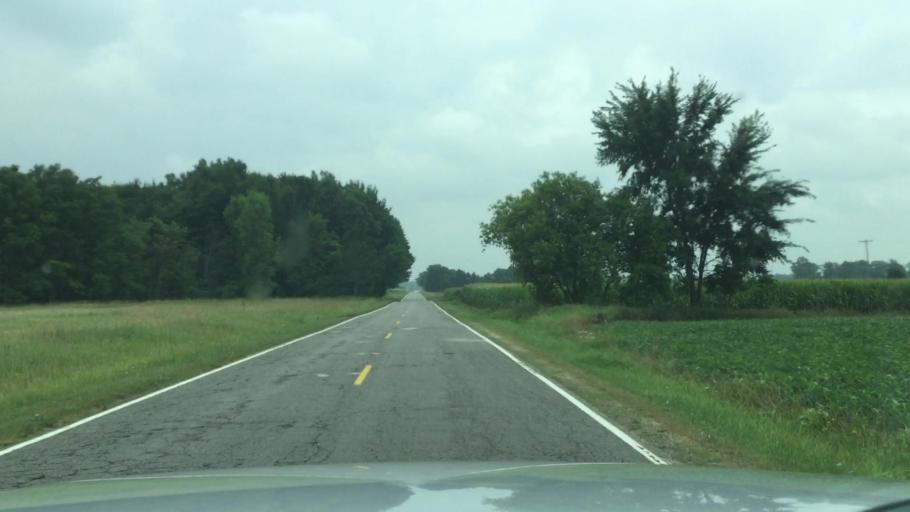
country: US
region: Michigan
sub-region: Shiawassee County
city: New Haven
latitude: 43.0785
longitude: -84.2261
